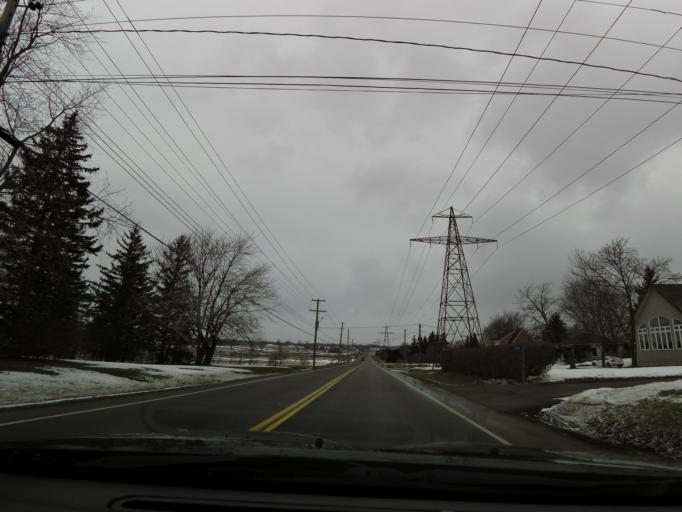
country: CA
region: Ontario
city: Ancaster
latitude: 43.2913
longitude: -79.9469
